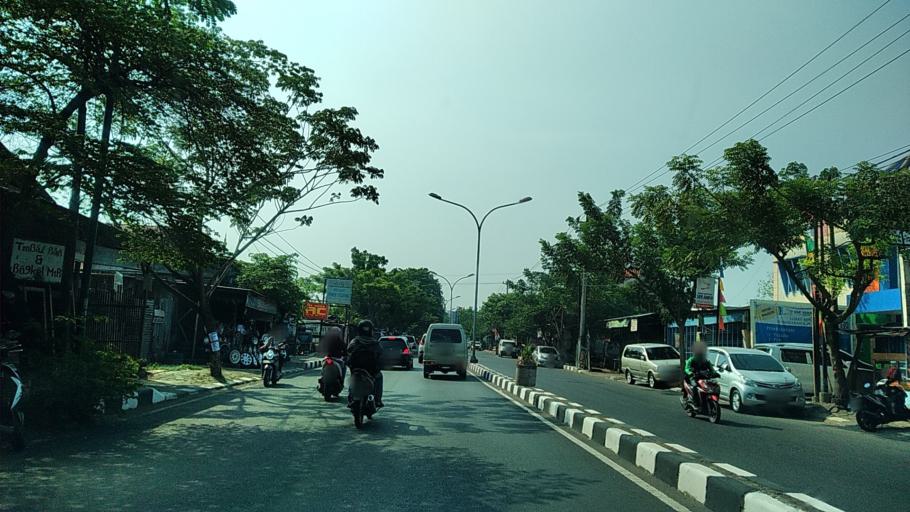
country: ID
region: Central Java
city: Semarang
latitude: -7.0227
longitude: 110.4581
